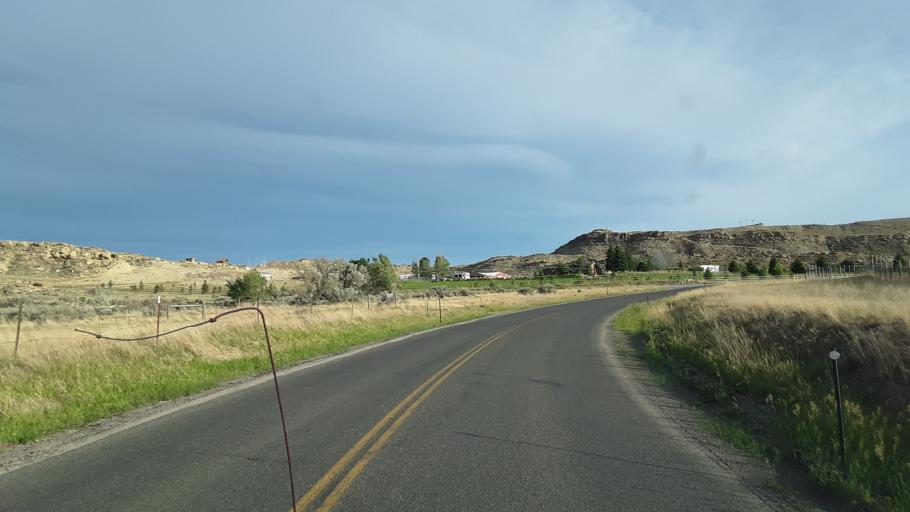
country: US
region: Wyoming
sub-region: Park County
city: Cody
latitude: 44.5276
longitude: -109.0084
